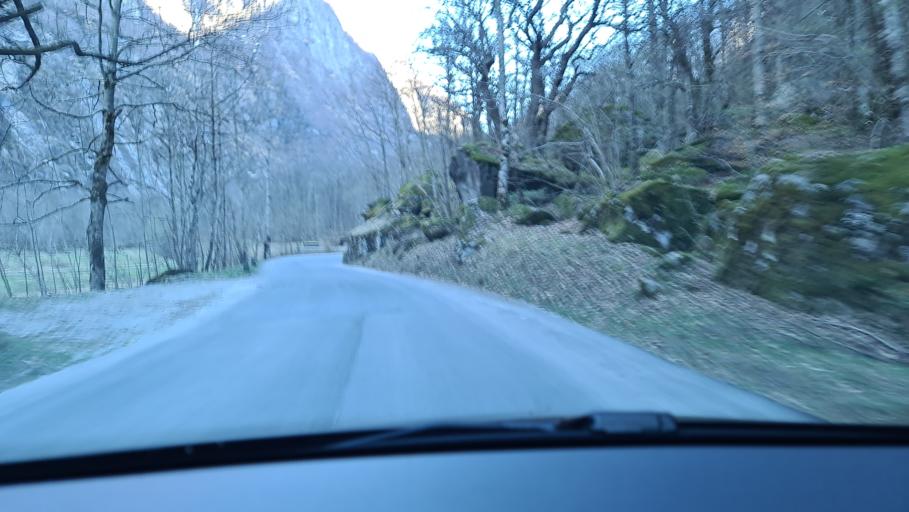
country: CH
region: Ticino
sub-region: Vallemaggia District
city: Cevio
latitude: 46.3979
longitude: 8.5334
